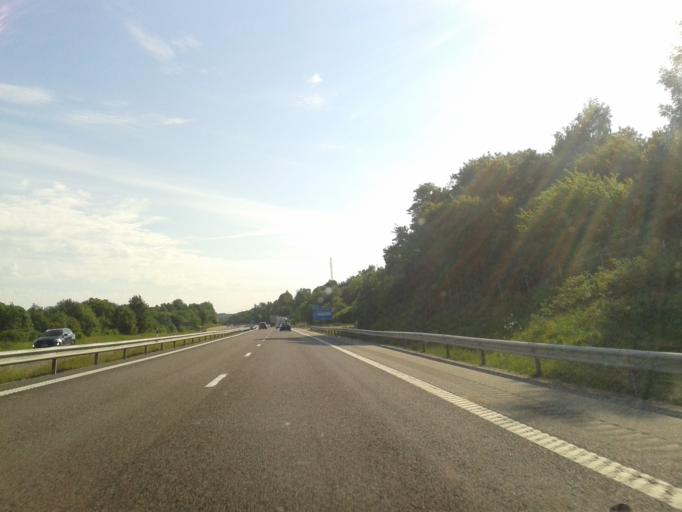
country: SE
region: Vaestra Goetaland
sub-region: Stenungsunds Kommun
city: Stora Hoga
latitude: 58.0492
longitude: 11.8623
